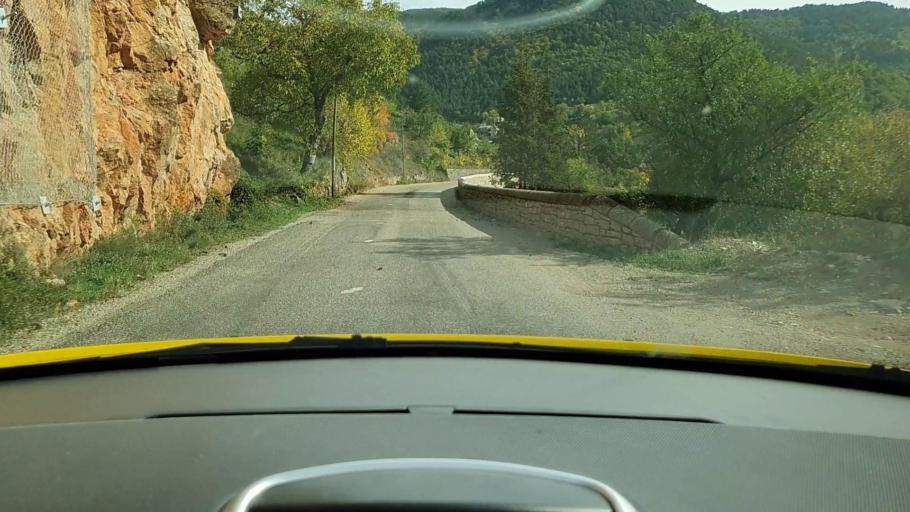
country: FR
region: Languedoc-Roussillon
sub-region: Departement de la Lozere
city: Meyrueis
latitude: 44.0789
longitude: 3.3829
